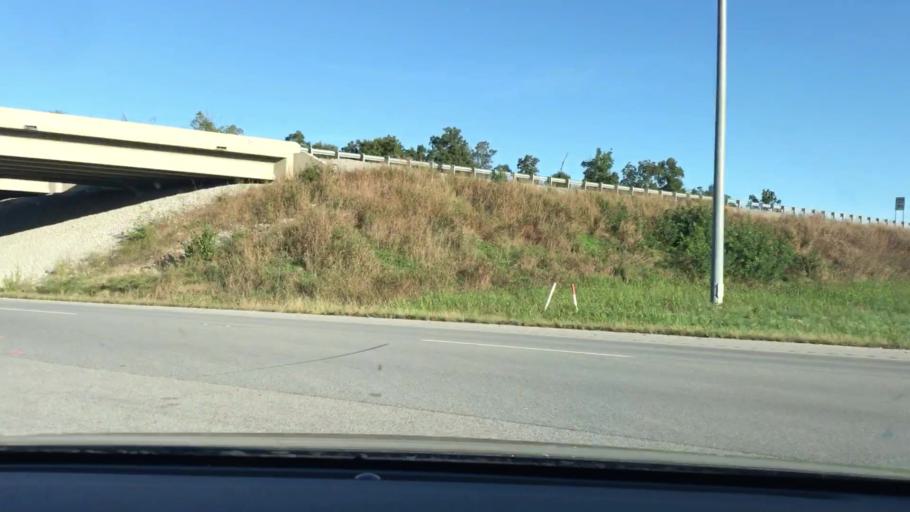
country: US
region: Kentucky
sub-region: Christian County
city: Hopkinsville
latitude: 36.8180
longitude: -87.4818
